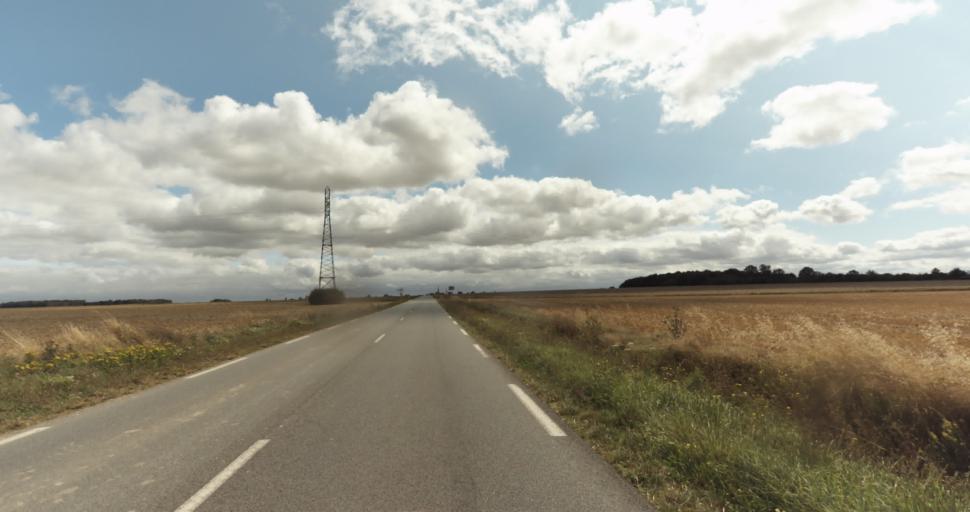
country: FR
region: Haute-Normandie
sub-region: Departement de l'Eure
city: Evreux
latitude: 48.9357
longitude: 1.2344
